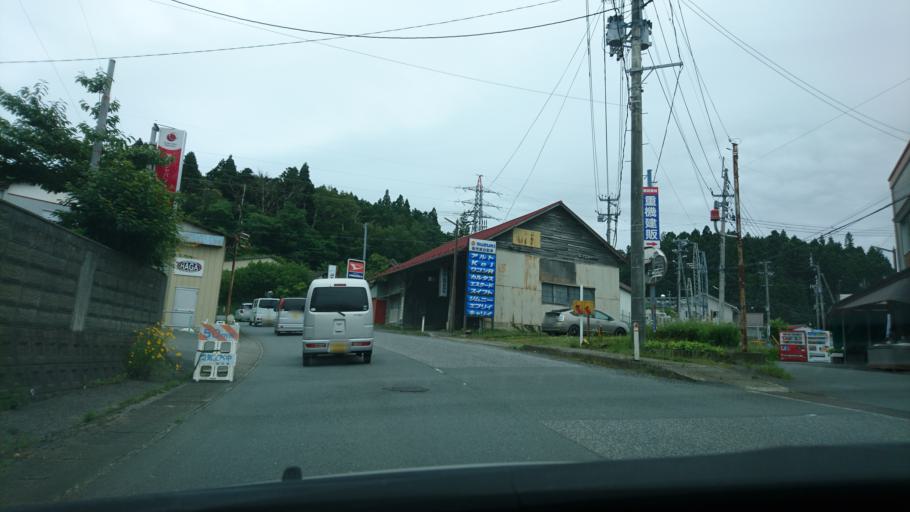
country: JP
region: Miyagi
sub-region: Oshika Gun
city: Onagawa Cho
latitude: 38.7882
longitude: 141.5056
